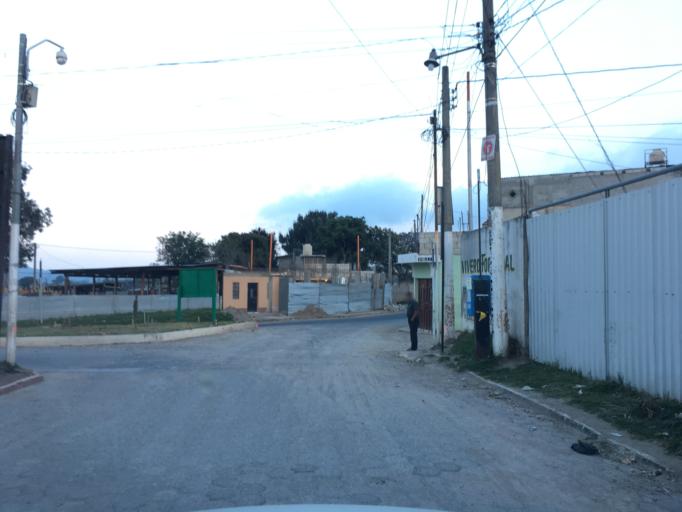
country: GT
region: Chimaltenango
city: Tecpan Guatemala
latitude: 14.7573
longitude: -91.0002
